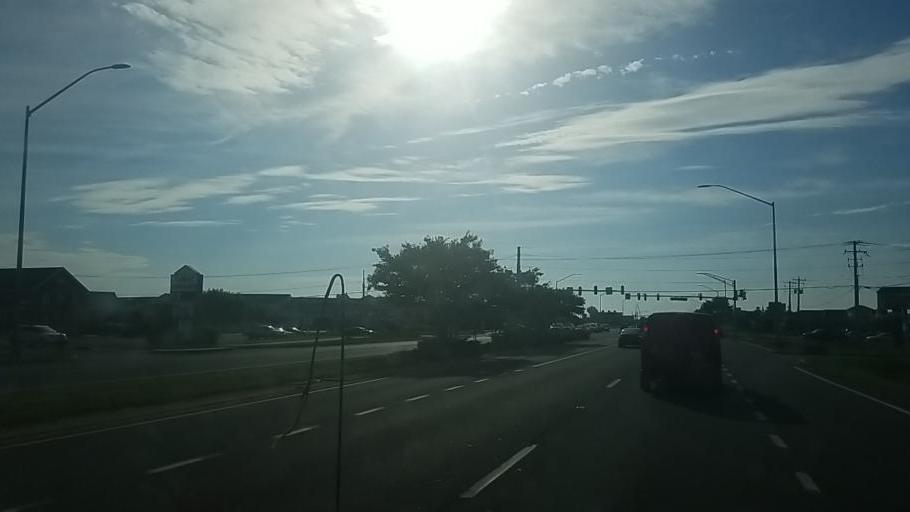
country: US
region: Maryland
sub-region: Worcester County
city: West Ocean City
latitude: 38.3363
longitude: -75.1064
